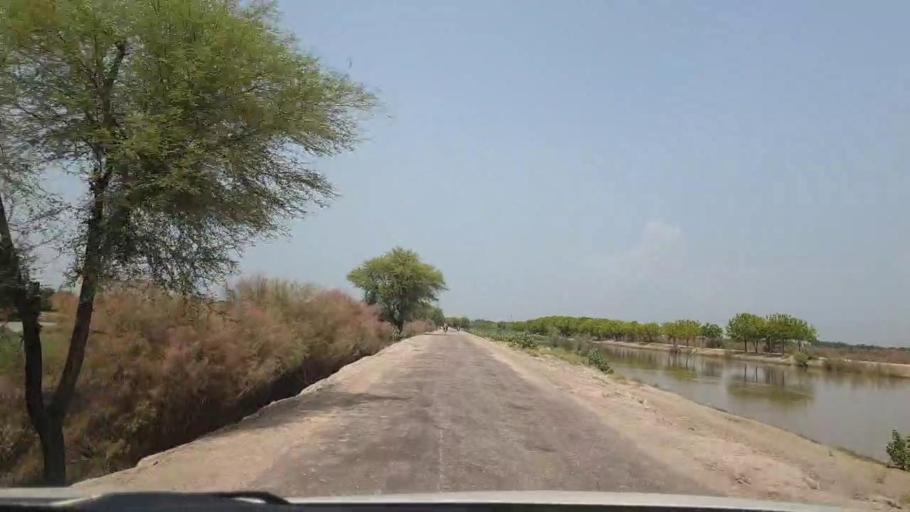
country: PK
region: Sindh
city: Dokri
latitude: 27.3509
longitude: 68.1124
